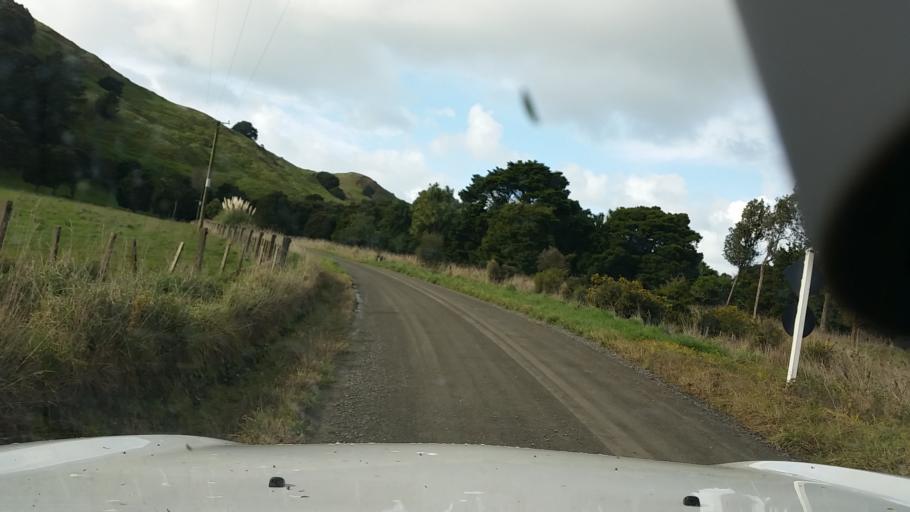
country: NZ
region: Wellington
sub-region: Masterton District
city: Masterton
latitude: -41.1855
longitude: 175.9445
